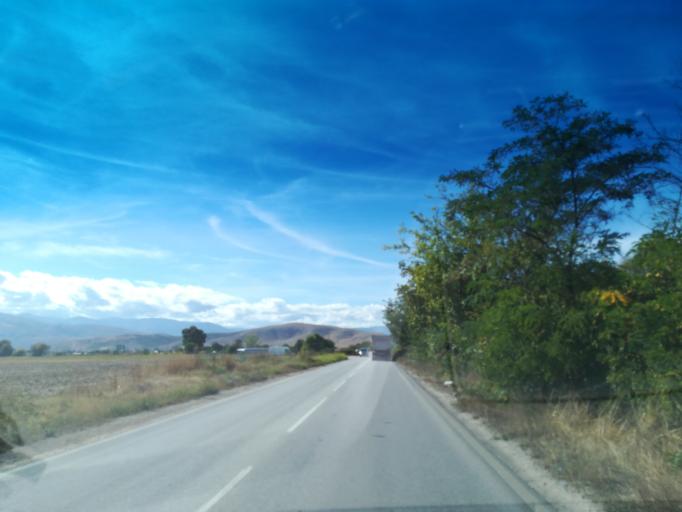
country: BG
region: Plovdiv
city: Stamboliyski
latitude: 42.1111
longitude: 24.5141
